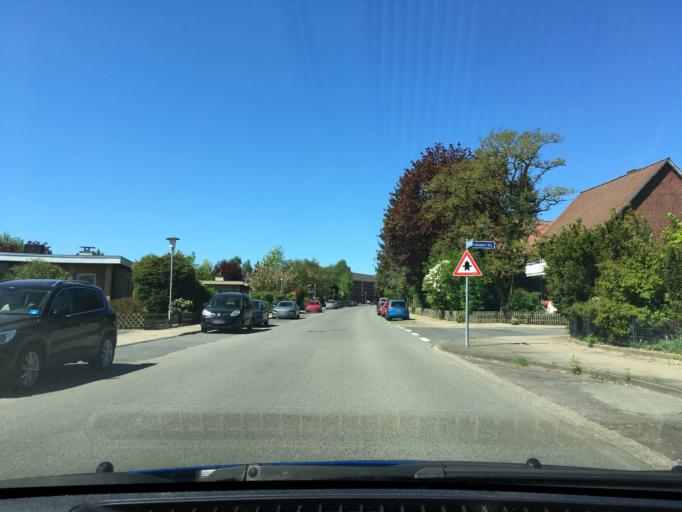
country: DE
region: Lower Saxony
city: Lueneburg
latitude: 53.2577
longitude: 10.3972
